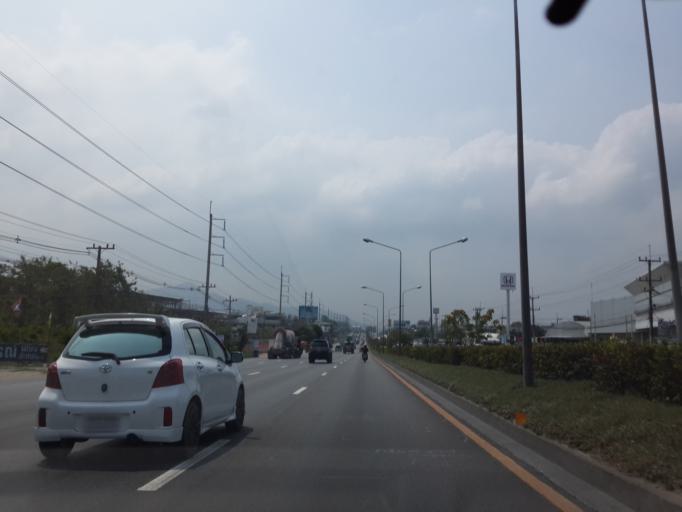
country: TH
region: Chon Buri
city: Chon Buri
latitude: 13.3744
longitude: 101.0196
